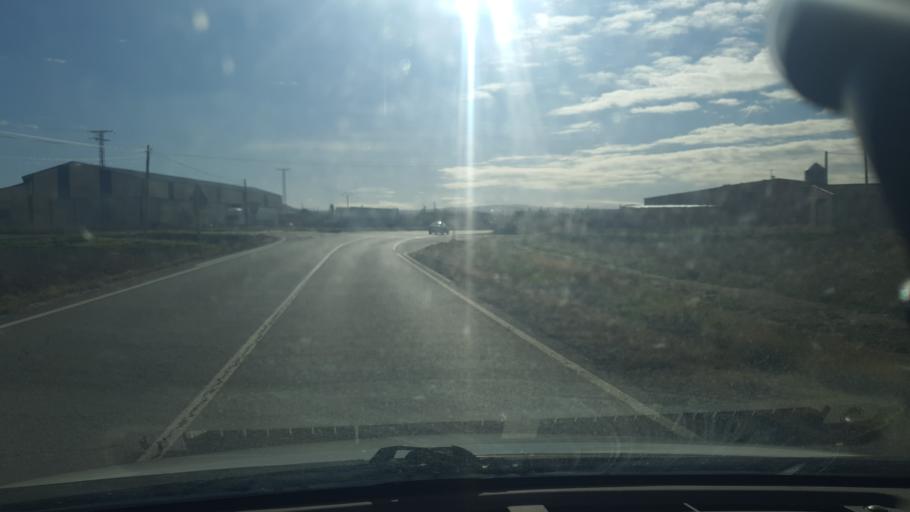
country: ES
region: Castille and Leon
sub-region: Provincia de Avila
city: Gotarrendura
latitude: 40.8035
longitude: -4.7592
